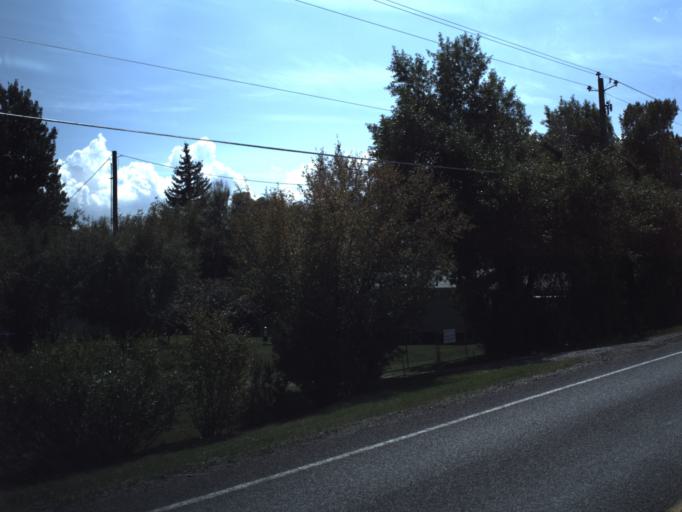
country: US
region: Idaho
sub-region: Bear Lake County
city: Paris
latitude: 41.9329
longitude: -111.3950
